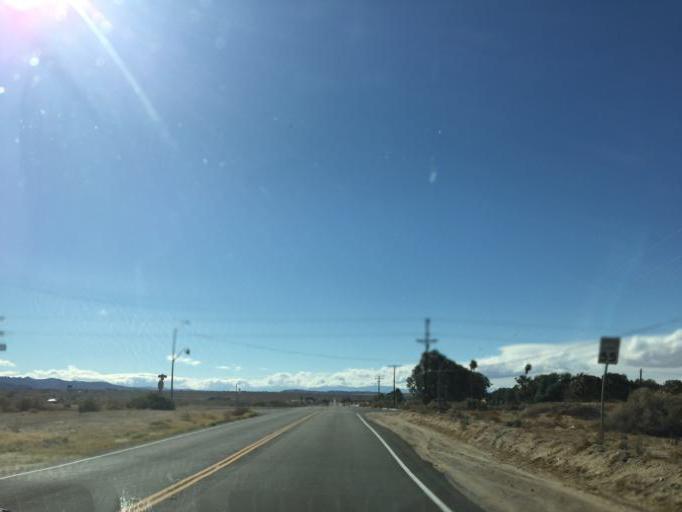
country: US
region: California
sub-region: San Bernardino County
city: Twentynine Palms
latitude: 34.1650
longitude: -116.0355
